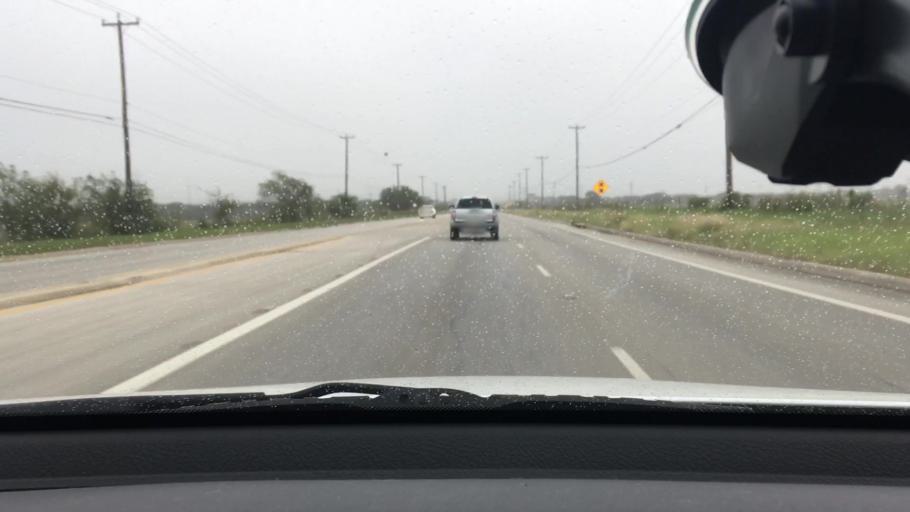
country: US
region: Texas
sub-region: Bexar County
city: Selma
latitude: 29.6018
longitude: -98.3326
